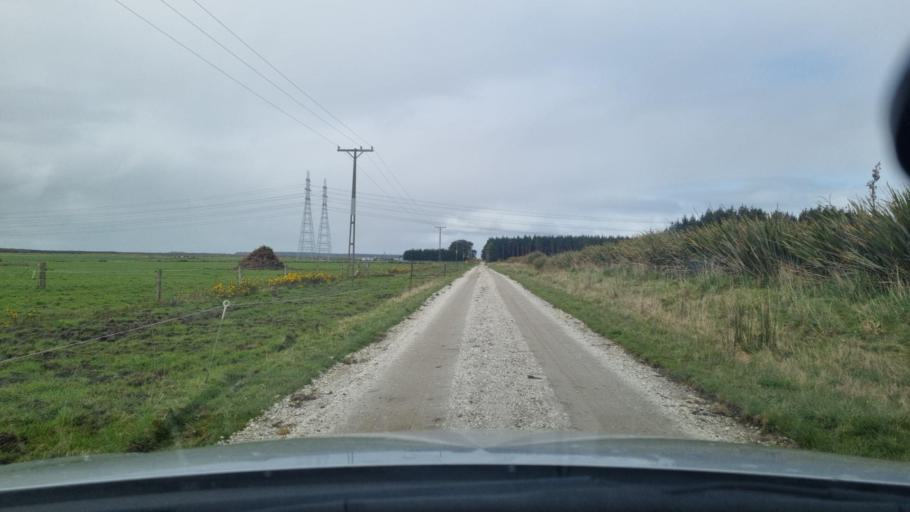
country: NZ
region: Southland
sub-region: Invercargill City
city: Invercargill
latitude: -46.4919
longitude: 168.4308
